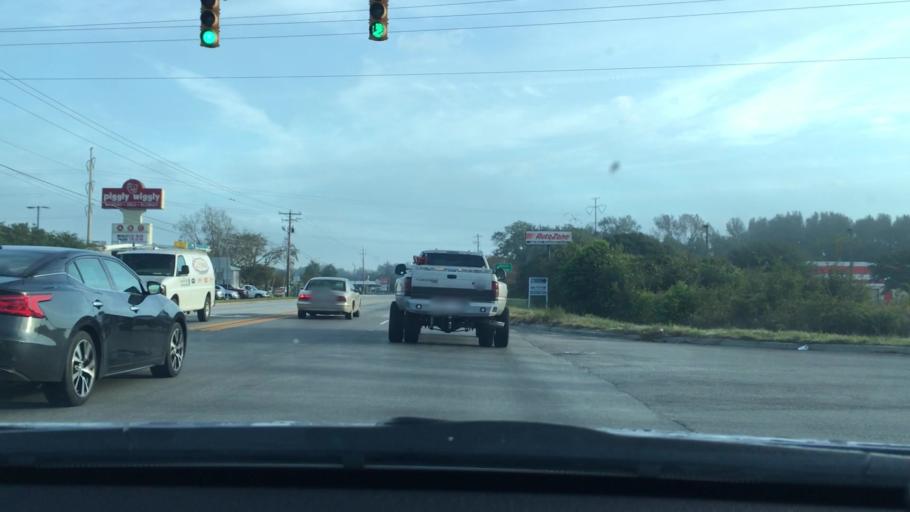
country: US
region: South Carolina
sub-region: Sumter County
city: South Sumter
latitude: 33.8841
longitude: -80.3488
